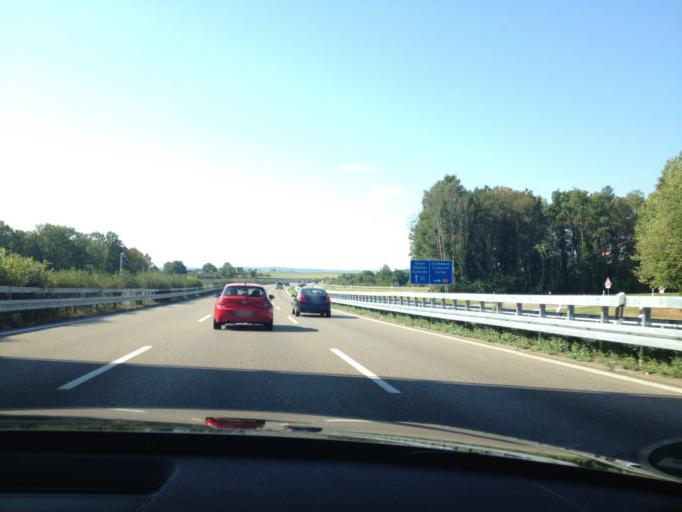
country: DE
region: Baden-Wuerttemberg
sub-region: Regierungsbezirk Stuttgart
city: Korntal
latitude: 48.8512
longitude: 9.1208
